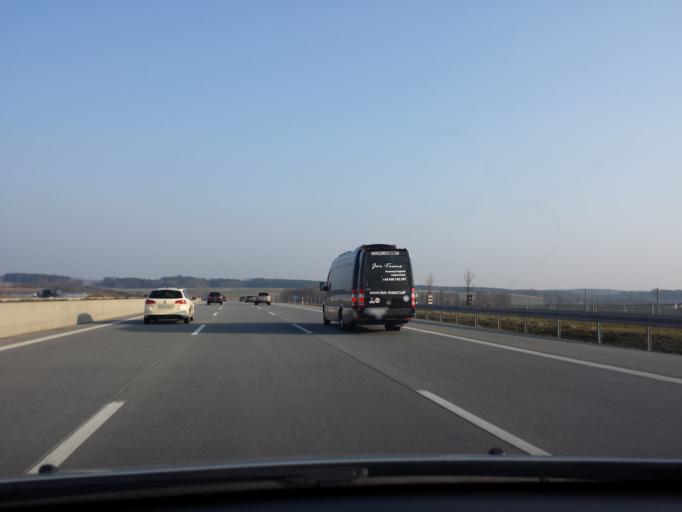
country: DE
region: Bavaria
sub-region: Upper Bavaria
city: Odelzhausen
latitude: 48.3002
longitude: 11.2187
